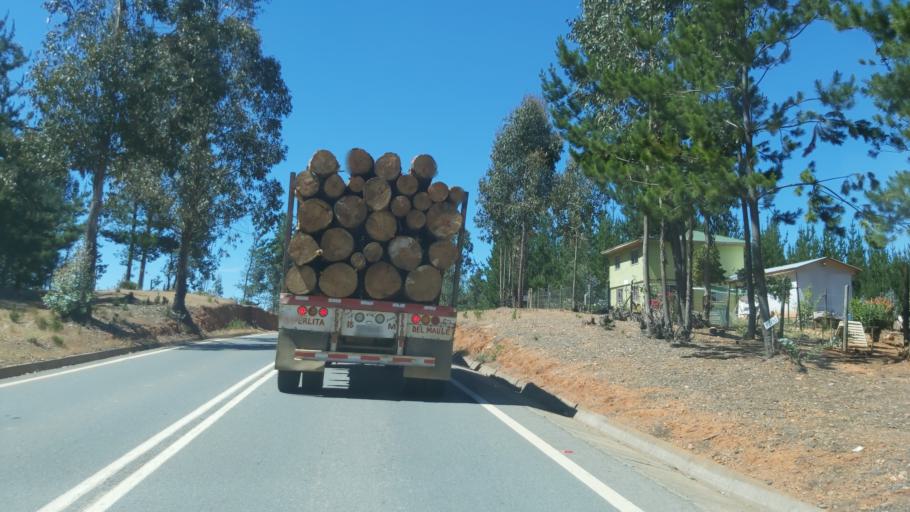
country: CL
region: Maule
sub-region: Provincia de Talca
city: Constitucion
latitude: -34.9329
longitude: -71.9863
